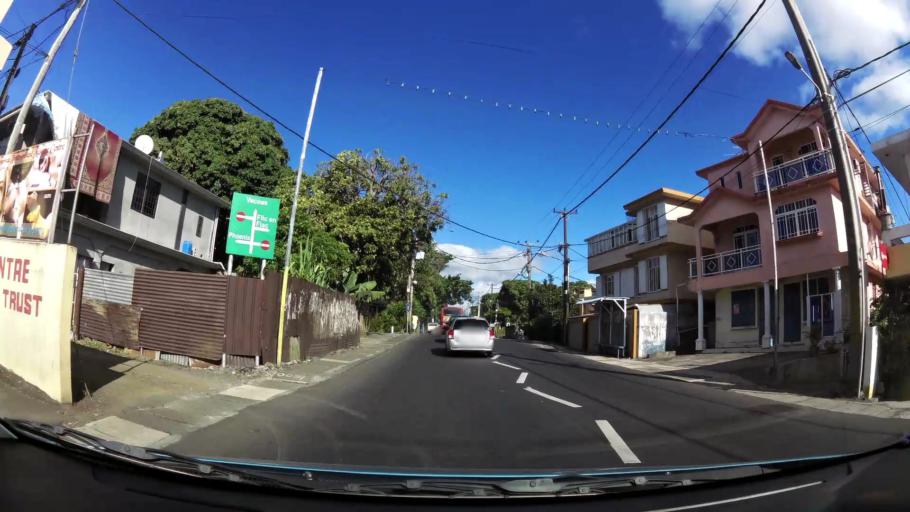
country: MU
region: Plaines Wilhems
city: Vacoas
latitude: -20.2823
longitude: 57.4790
